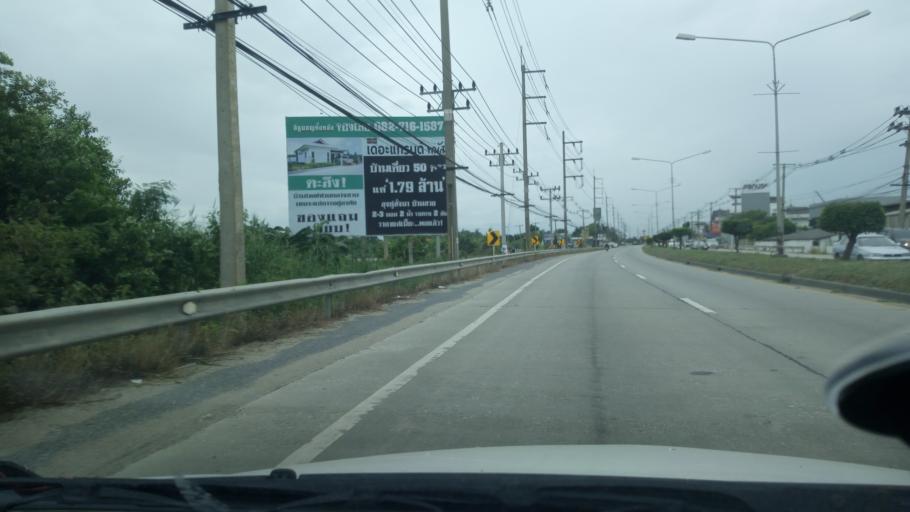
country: TH
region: Chon Buri
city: Phanat Nikhom
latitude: 13.4437
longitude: 101.1524
